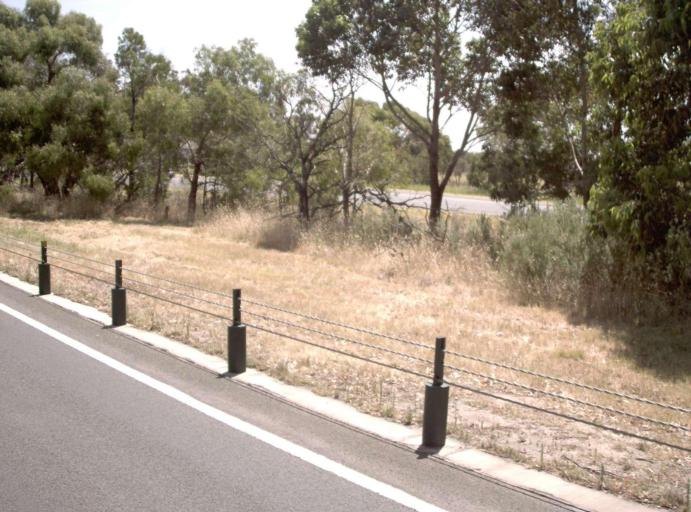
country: AU
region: Victoria
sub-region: Casey
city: Tooradin
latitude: -38.2140
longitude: 145.4163
